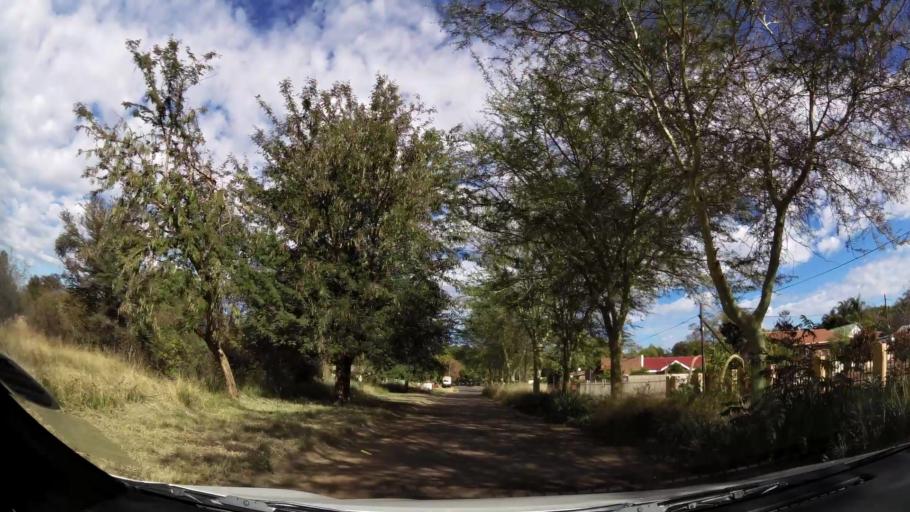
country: ZA
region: Limpopo
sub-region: Waterberg District Municipality
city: Bela-Bela
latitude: -24.8769
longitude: 28.2933
